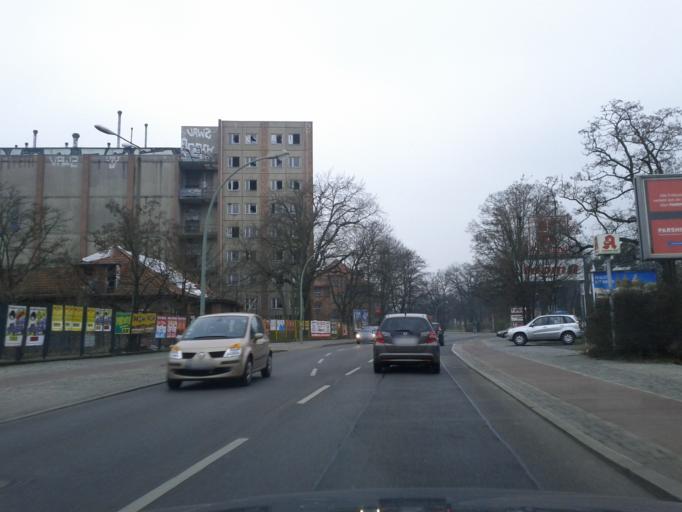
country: DE
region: Berlin
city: Berlin Koepenick
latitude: 52.4514
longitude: 13.5873
